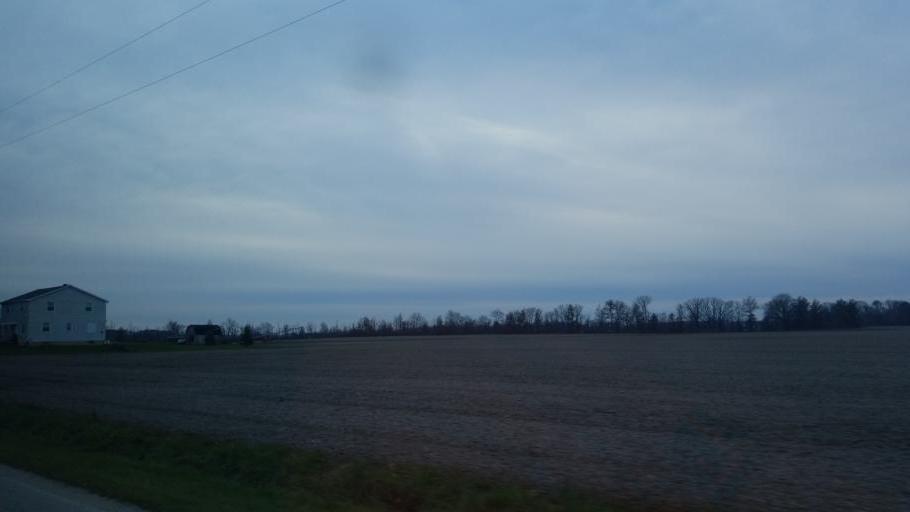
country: US
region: Indiana
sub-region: Adams County
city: Decatur
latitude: 40.7725
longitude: -84.8799
